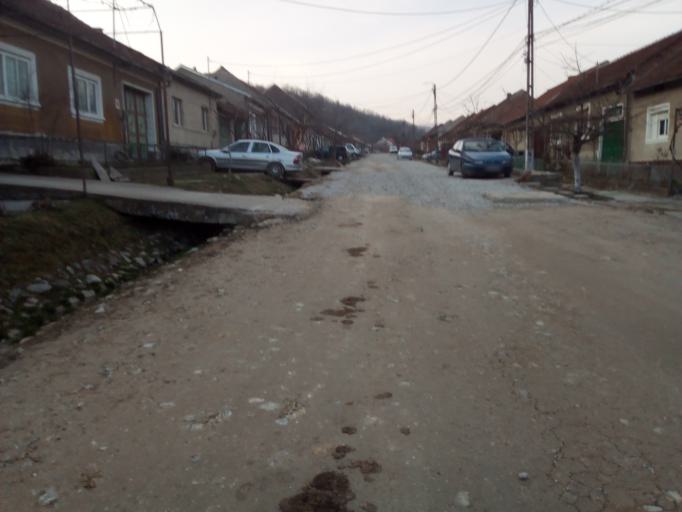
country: RO
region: Mehedinti
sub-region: Comuna Eselnita
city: Eselnita
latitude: 44.6948
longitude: 22.3633
